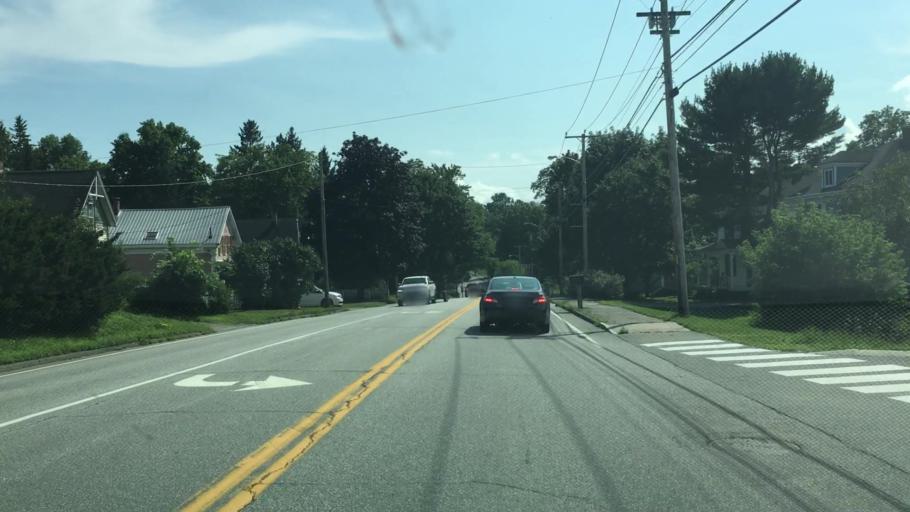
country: US
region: Maine
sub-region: Penobscot County
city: Hampden
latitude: 44.7379
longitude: -68.8398
